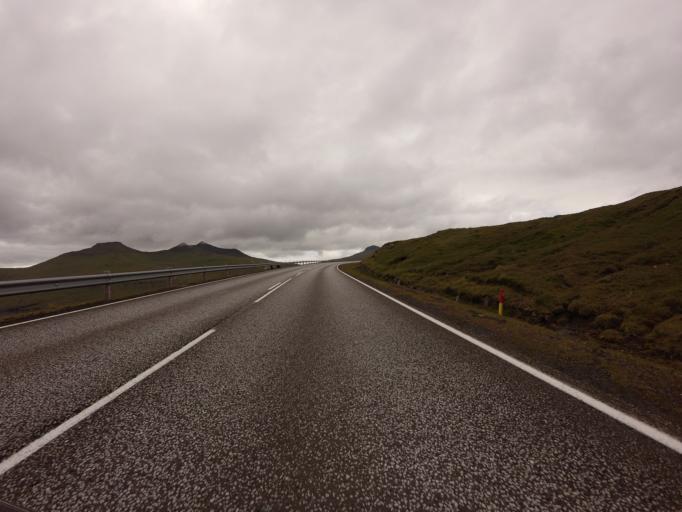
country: FO
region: Streymoy
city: Vestmanna
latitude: 62.1165
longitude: -7.1031
